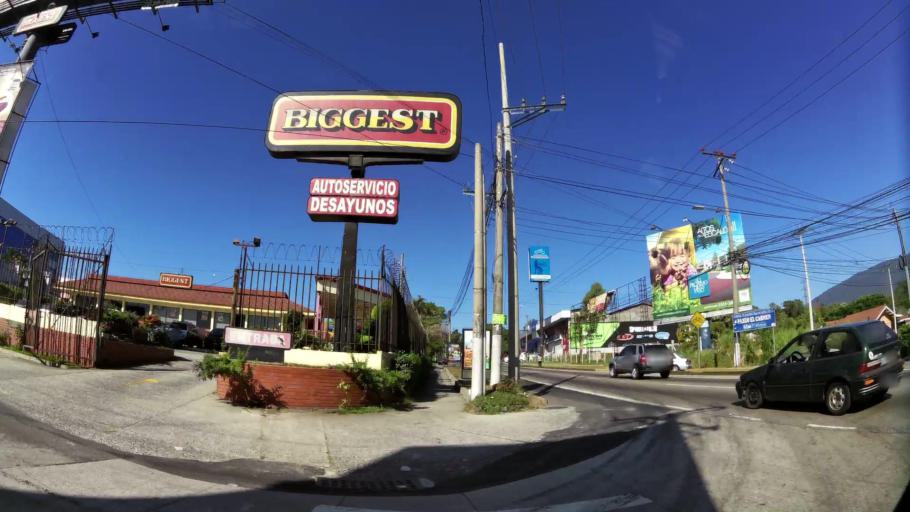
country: SV
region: La Libertad
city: Santa Tecla
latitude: 13.6721
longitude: -89.2763
